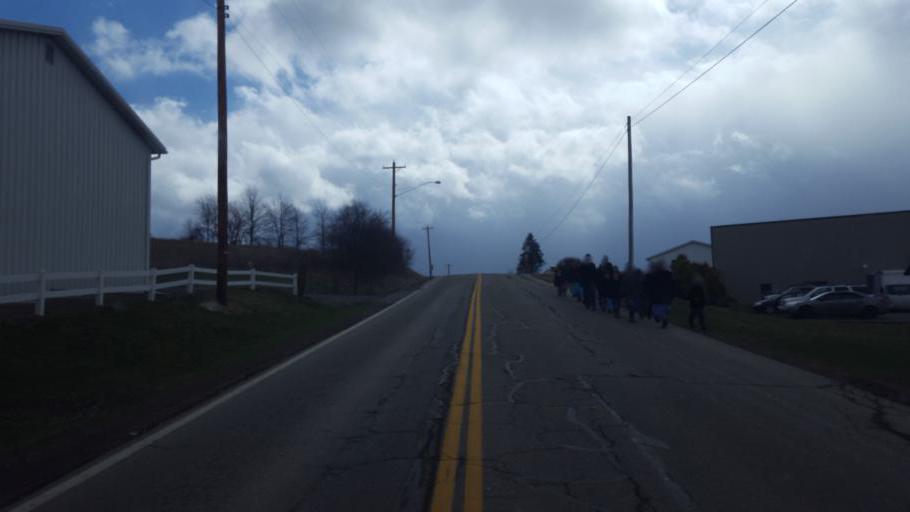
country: US
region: Ohio
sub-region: Tuscarawas County
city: Sugarcreek
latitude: 40.4432
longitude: -81.7643
